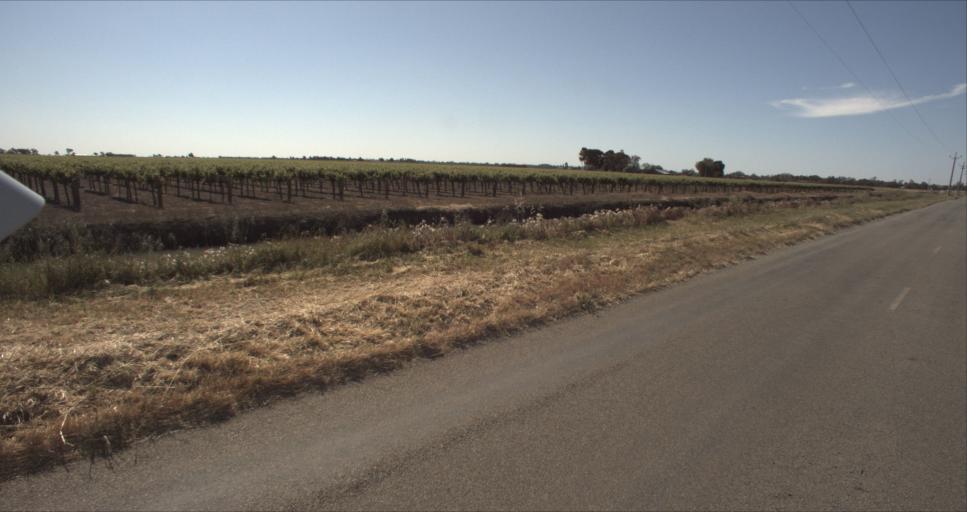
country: AU
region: New South Wales
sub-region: Leeton
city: Leeton
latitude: -34.5803
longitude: 146.3800
